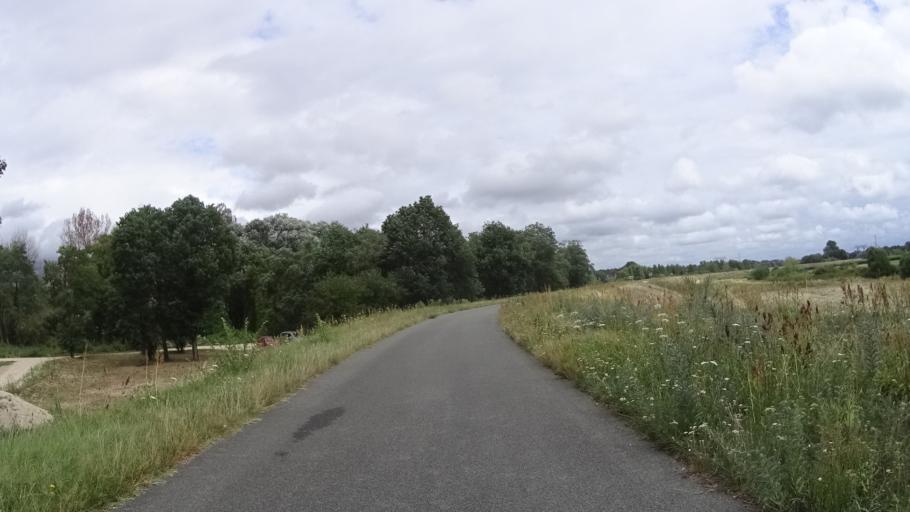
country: FR
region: Centre
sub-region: Departement du Loiret
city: Mareau-aux-Pres
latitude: 47.8619
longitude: 1.7812
